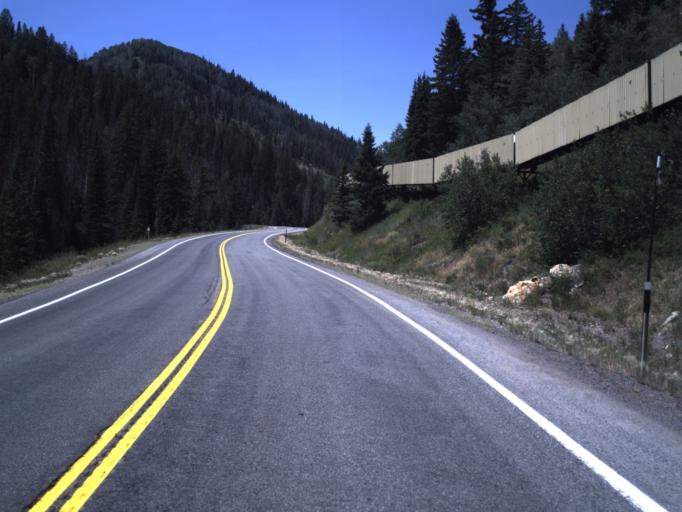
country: US
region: Utah
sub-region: Sanpete County
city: Fairview
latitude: 39.6831
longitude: -111.1720
